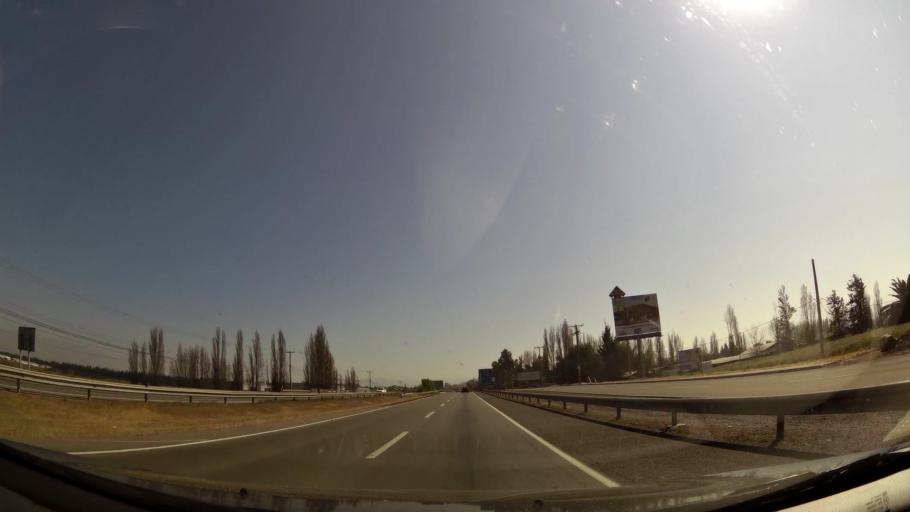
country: CL
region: Santiago Metropolitan
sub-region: Provincia de Chacabuco
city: Chicureo Abajo
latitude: -33.3019
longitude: -70.6998
